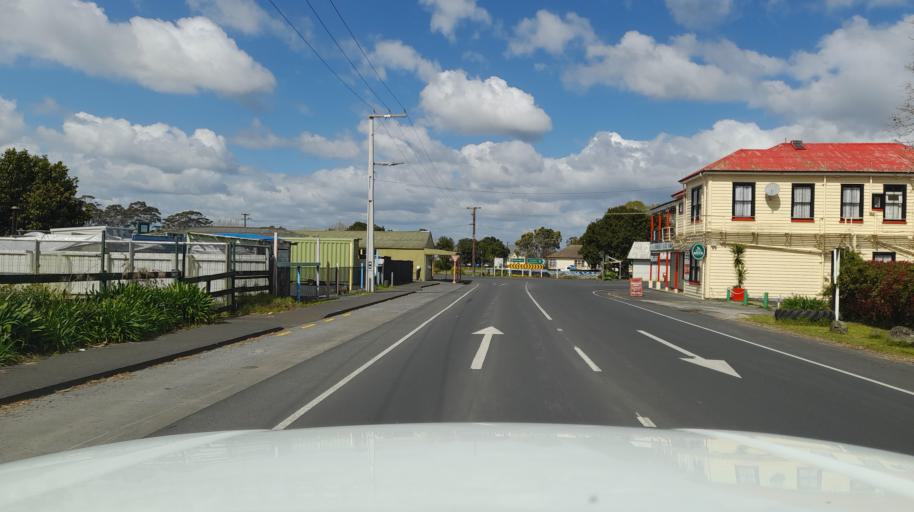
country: NZ
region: Northland
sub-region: Far North District
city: Waimate North
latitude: -35.3514
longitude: 173.8814
